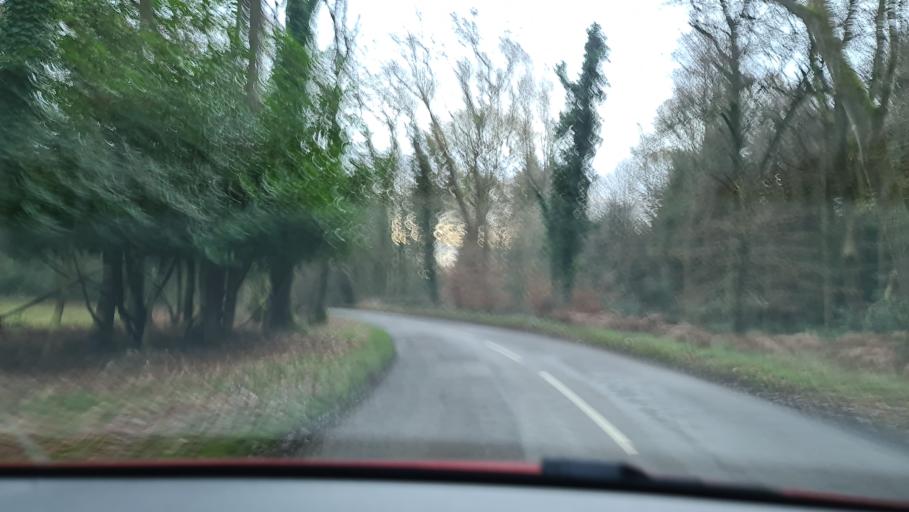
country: GB
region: England
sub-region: Buckinghamshire
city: Princes Risborough
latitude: 51.7072
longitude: -0.7844
